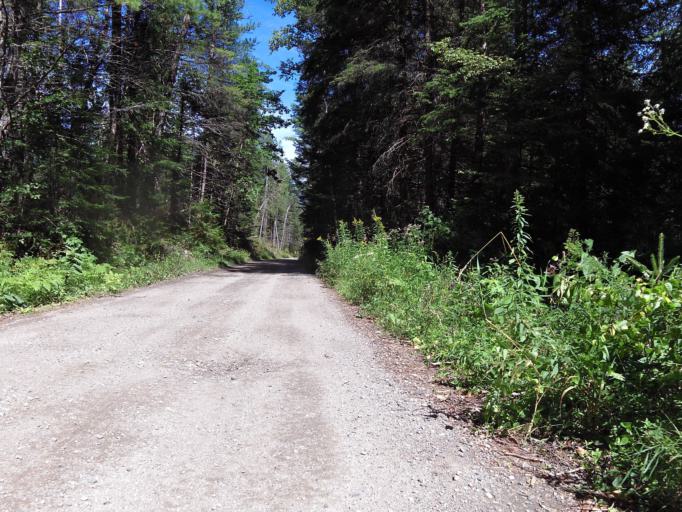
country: CA
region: Ontario
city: Renfrew
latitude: 45.0873
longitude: -76.7207
